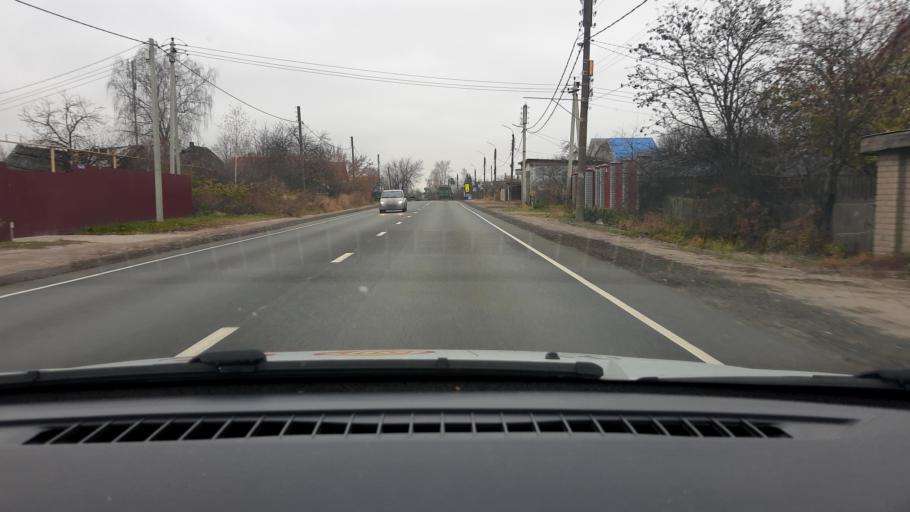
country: RU
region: Nizjnij Novgorod
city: Gidrotorf
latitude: 56.5363
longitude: 43.5378
